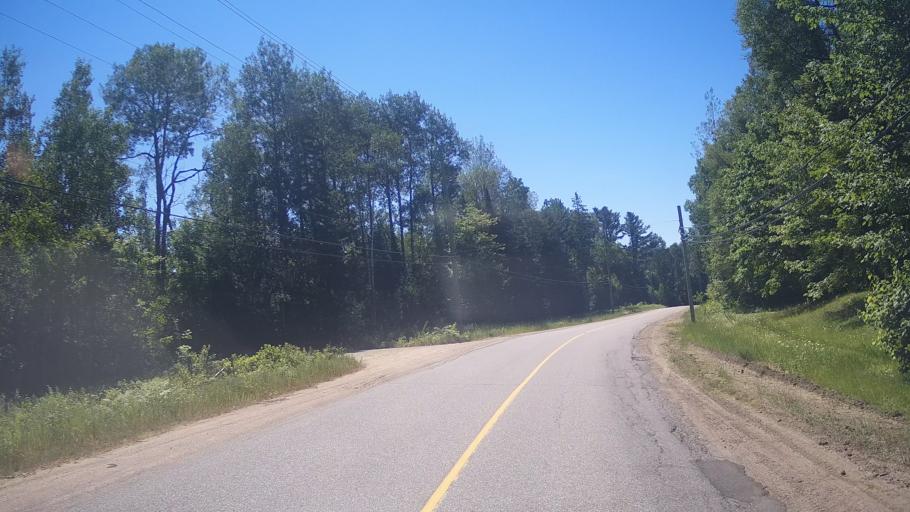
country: CA
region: Ontario
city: Huntsville
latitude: 45.3706
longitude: -79.2066
